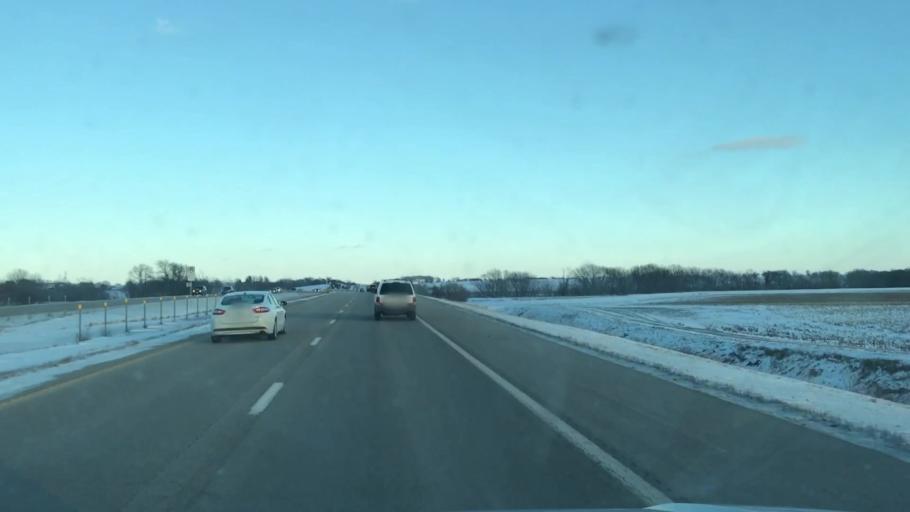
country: US
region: Missouri
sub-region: Buchanan County
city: Saint Joseph
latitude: 39.7478
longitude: -94.7313
